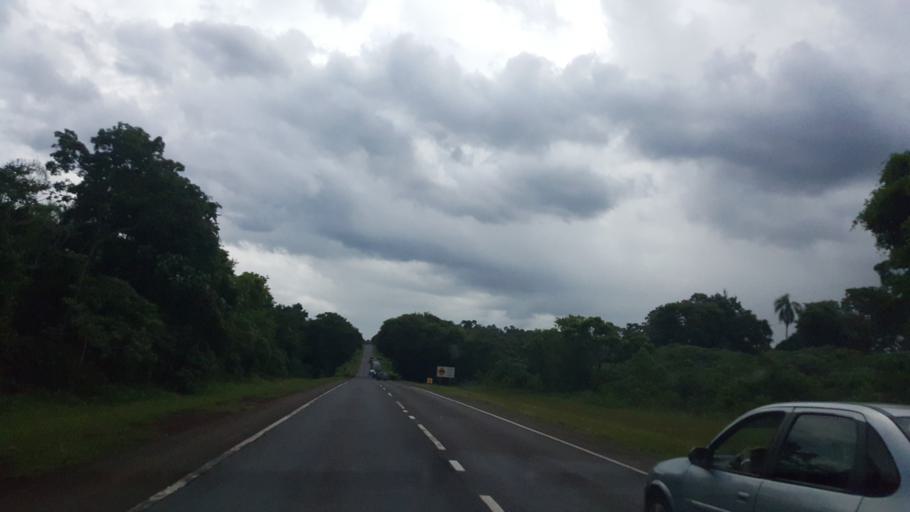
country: AR
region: Misiones
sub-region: Departamento de Iguazu
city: Puerto Iguazu
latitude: -25.7213
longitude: -54.5238
